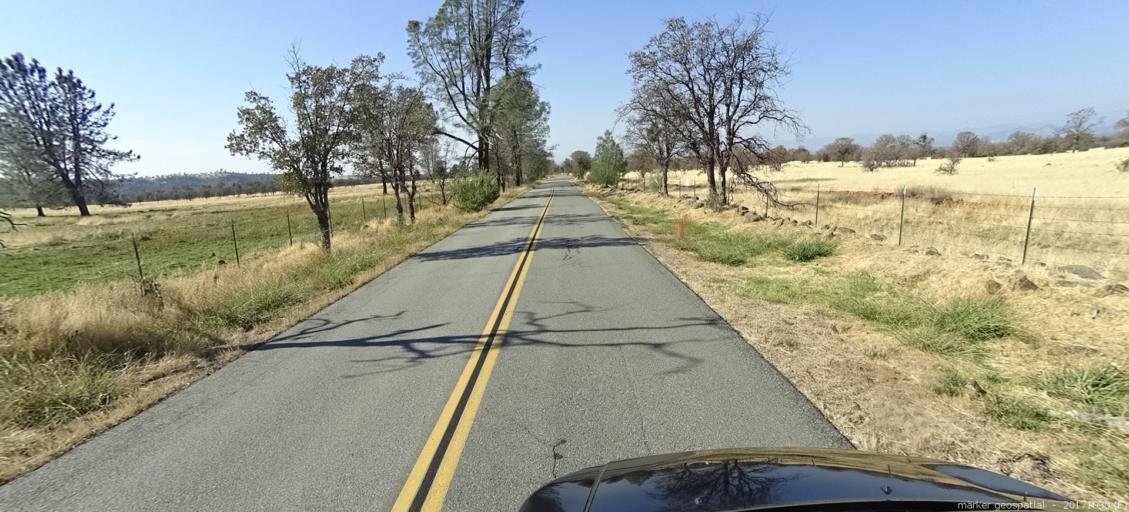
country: US
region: California
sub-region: Shasta County
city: Shingletown
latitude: 40.6364
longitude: -121.9687
